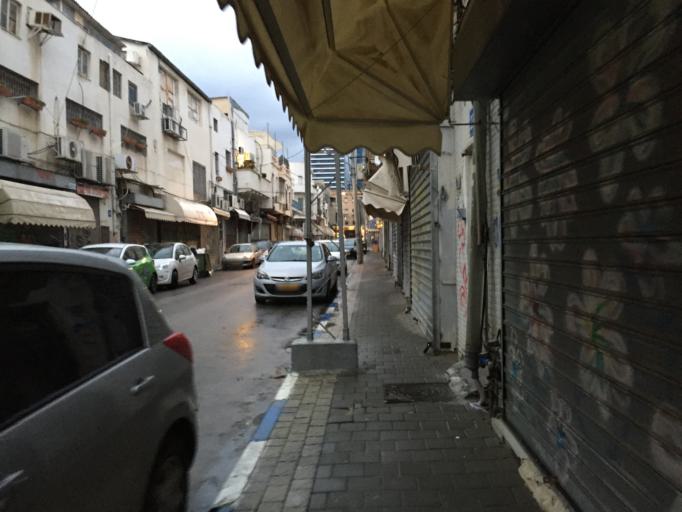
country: IL
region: Tel Aviv
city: Yafo
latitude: 32.0588
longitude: 34.7698
